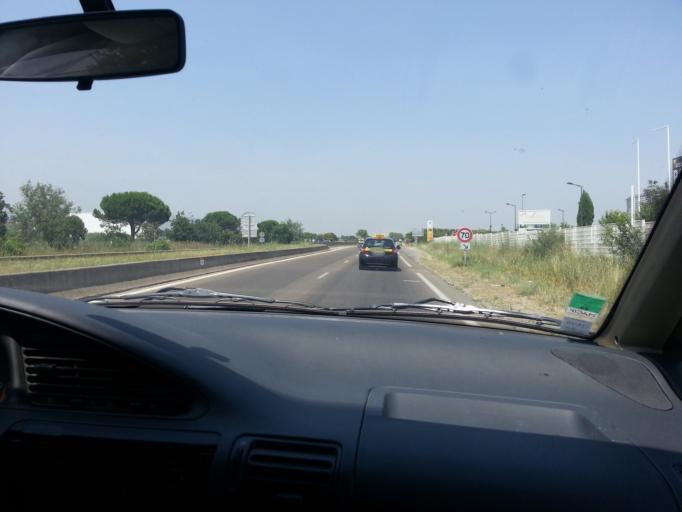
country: FR
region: Languedoc-Roussillon
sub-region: Departement de l'Herault
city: Perols
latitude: 43.5901
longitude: 3.9403
